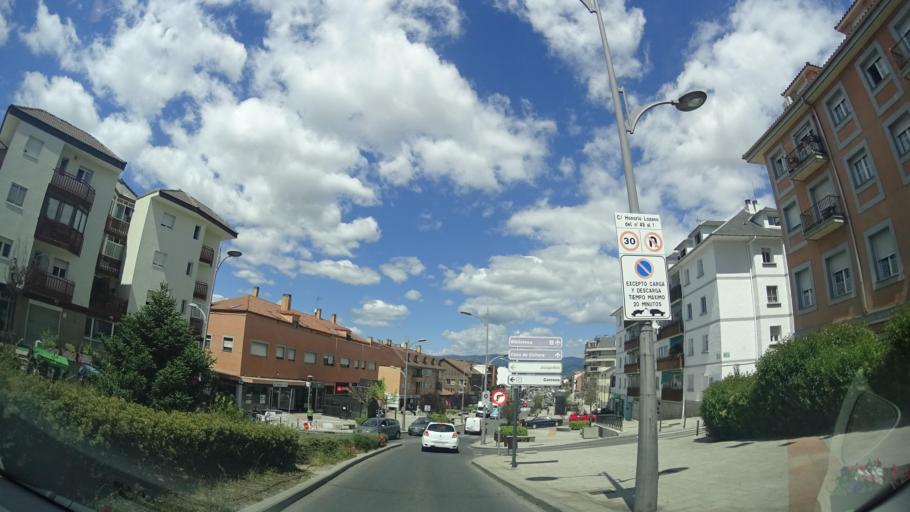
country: ES
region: Madrid
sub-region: Provincia de Madrid
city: Collado-Villalba
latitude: 40.6293
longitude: -4.0013
